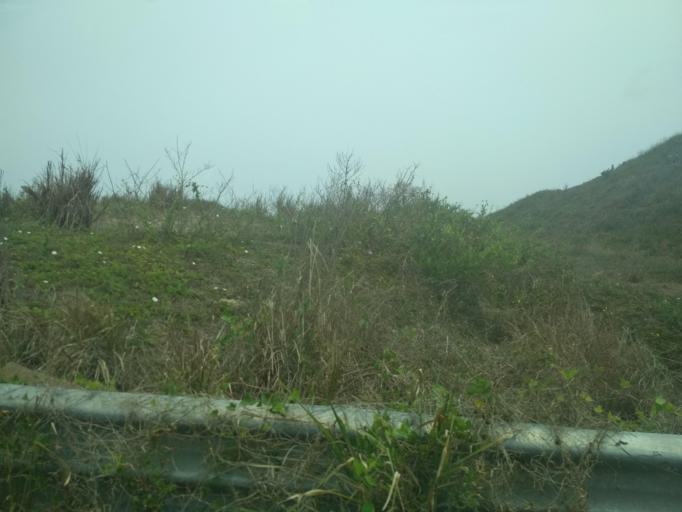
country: MX
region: Veracruz
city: Anton Lizardo
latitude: 19.0547
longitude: -96.0414
